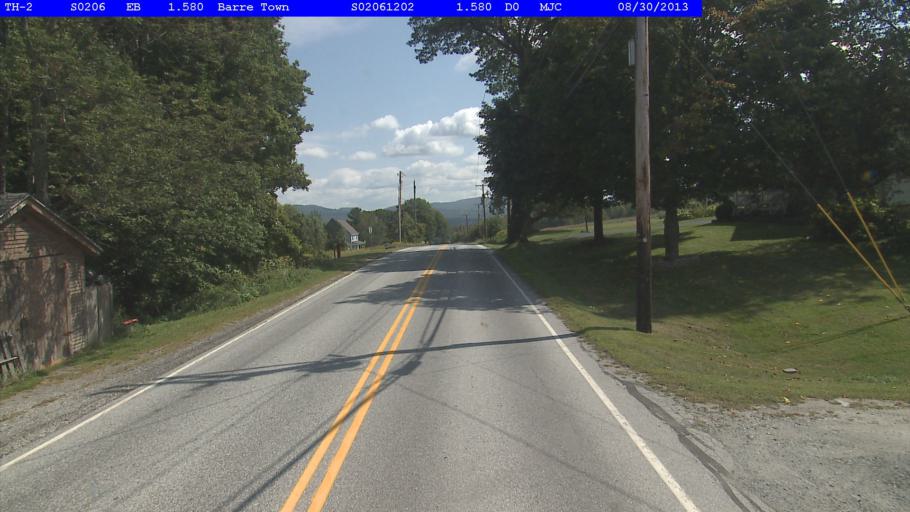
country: US
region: Vermont
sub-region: Washington County
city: South Barre
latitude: 44.1612
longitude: -72.4652
